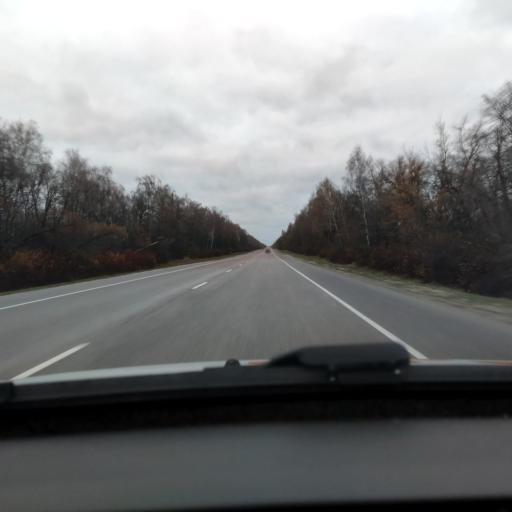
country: RU
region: Lipetsk
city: Khlevnoye
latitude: 52.2808
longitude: 39.1680
